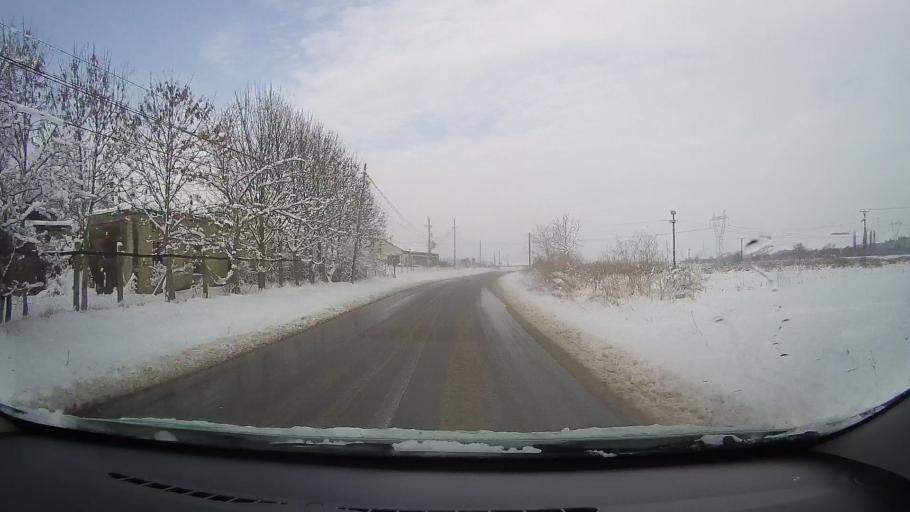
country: RO
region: Alba
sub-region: Comuna Pianu
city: Pianu de Jos
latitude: 45.9459
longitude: 23.4796
